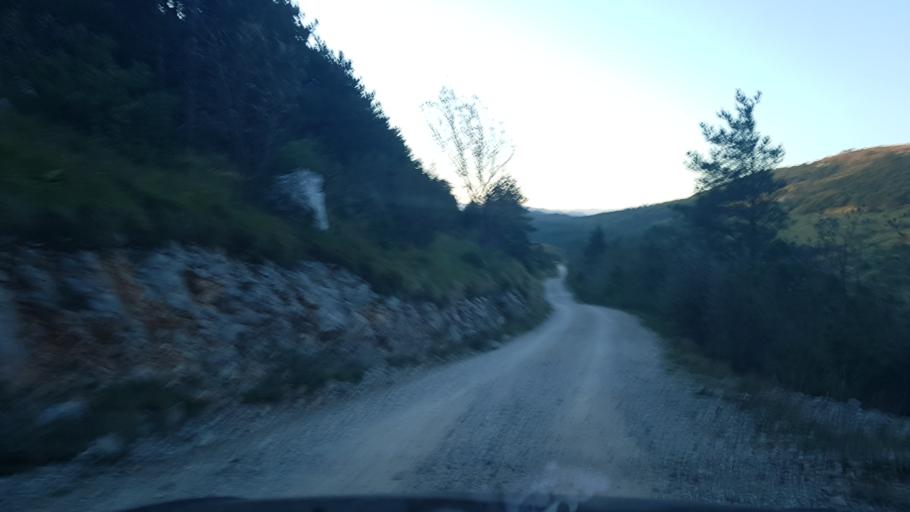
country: SI
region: Vipava
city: Vipava
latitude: 45.7899
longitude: 14.0225
